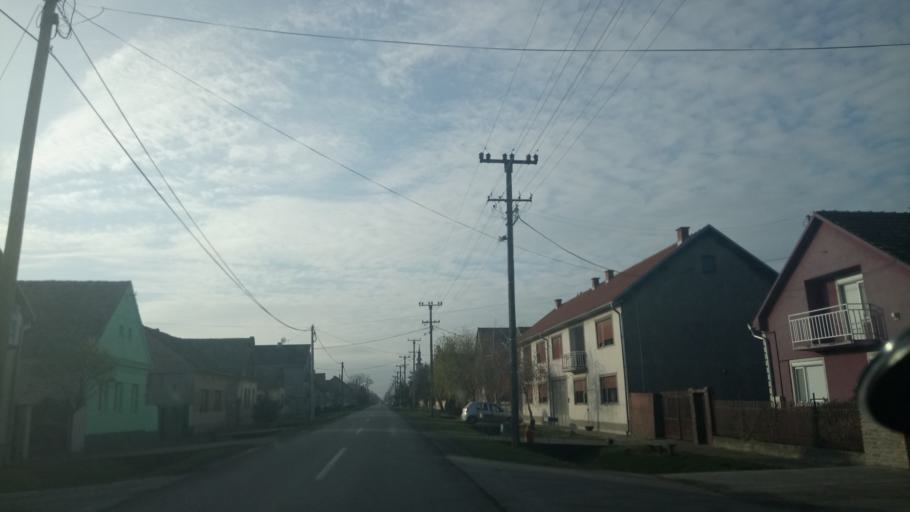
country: RS
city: Vojka
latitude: 44.9351
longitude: 20.1592
